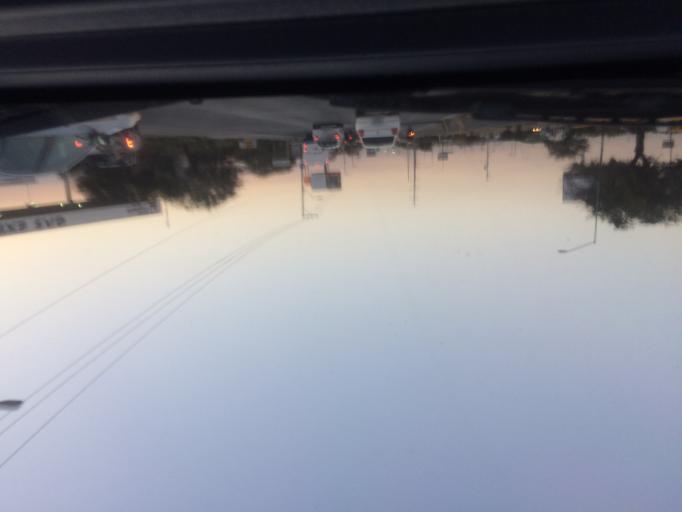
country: MX
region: Guanajuato
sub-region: Leon
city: Medina
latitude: 21.1448
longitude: -101.6338
